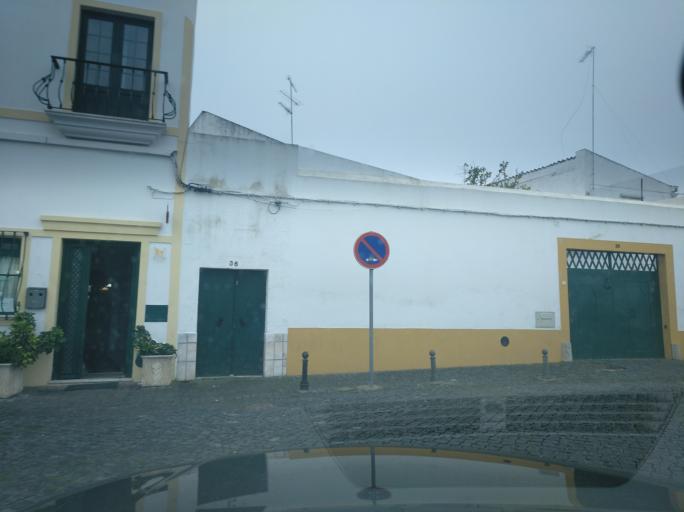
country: PT
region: Portalegre
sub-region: Campo Maior
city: Campo Maior
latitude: 39.0133
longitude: -7.0676
